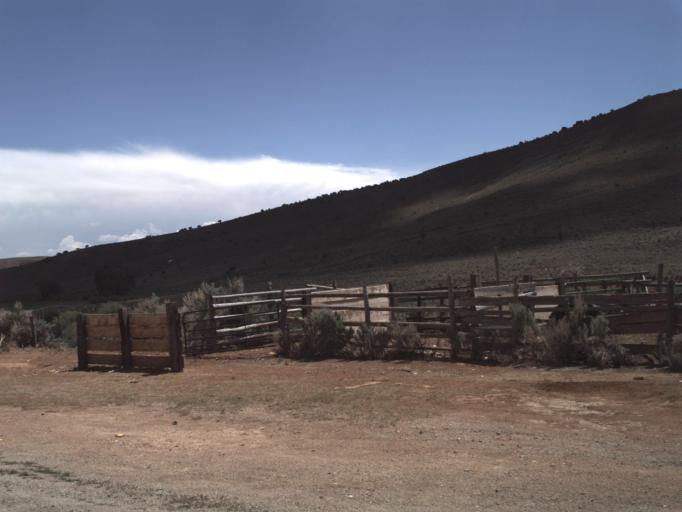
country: US
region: Utah
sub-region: Rich County
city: Randolph
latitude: 41.5005
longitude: -111.2781
